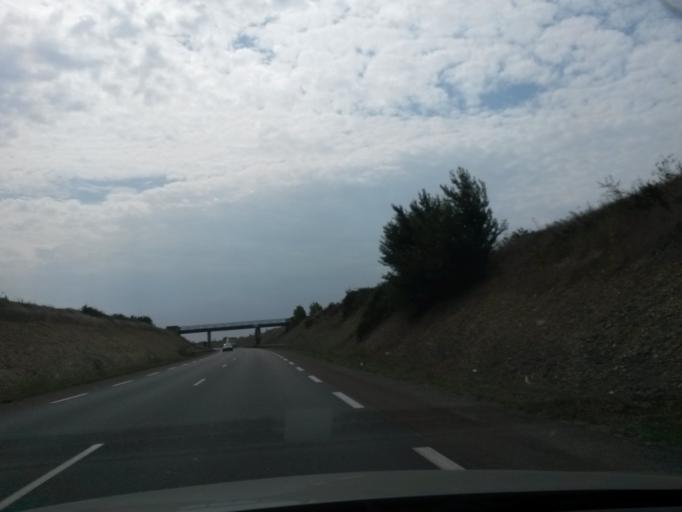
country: FR
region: Poitou-Charentes
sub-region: Departement de la Charente-Maritime
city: Saint-Xandre
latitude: 46.1865
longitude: -1.0936
